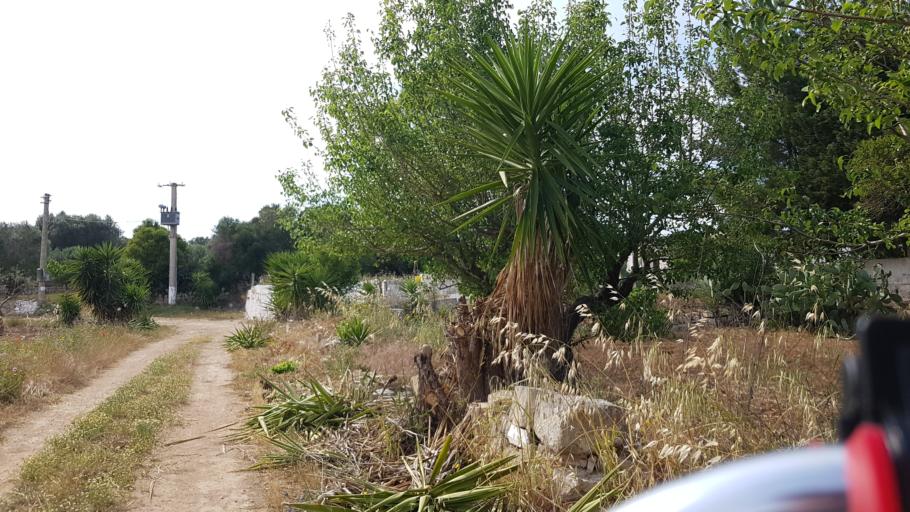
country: IT
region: Apulia
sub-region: Provincia di Brindisi
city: San Vito dei Normanni
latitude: 40.6564
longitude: 17.8018
